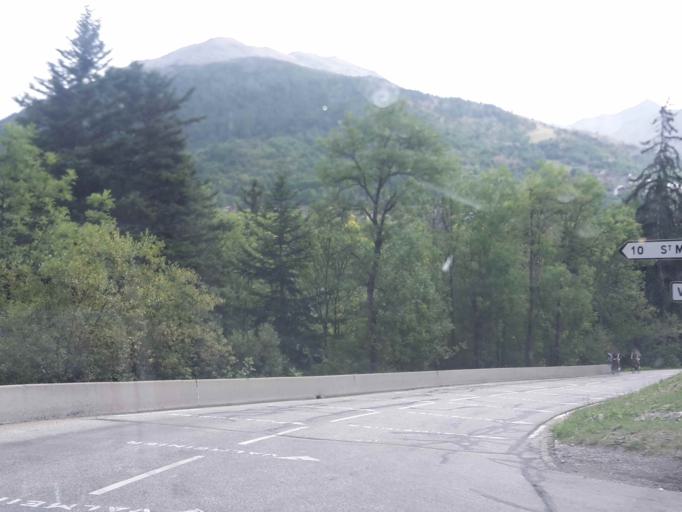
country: FR
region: Rhone-Alpes
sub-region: Departement de la Savoie
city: Saint-Michel-de-Maurienne
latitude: 45.1967
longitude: 6.4660
